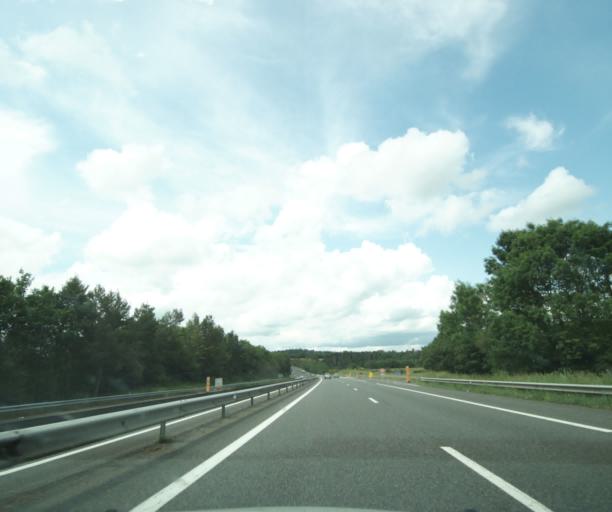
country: FR
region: Auvergne
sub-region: Departement de l'Allier
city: Bellenaves
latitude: 46.2309
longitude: 3.0996
